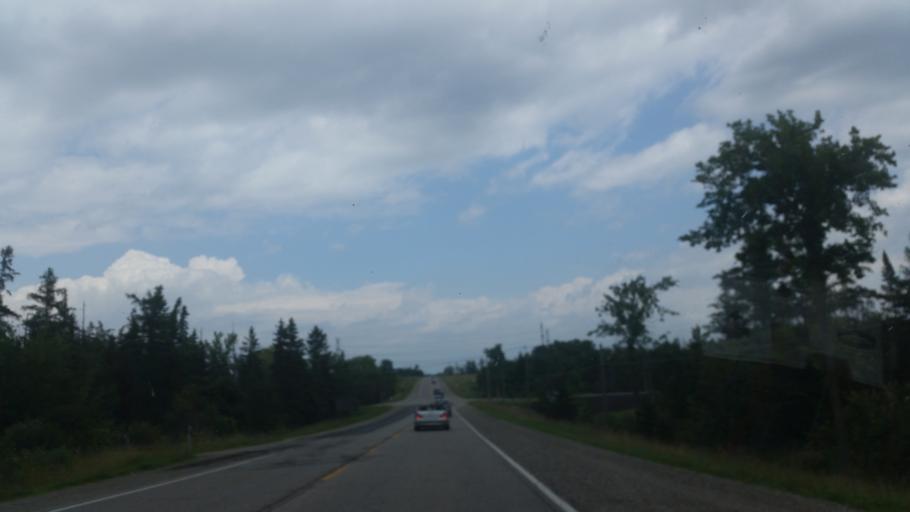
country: CA
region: Ontario
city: Orangeville
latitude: 43.7166
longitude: -80.1137
